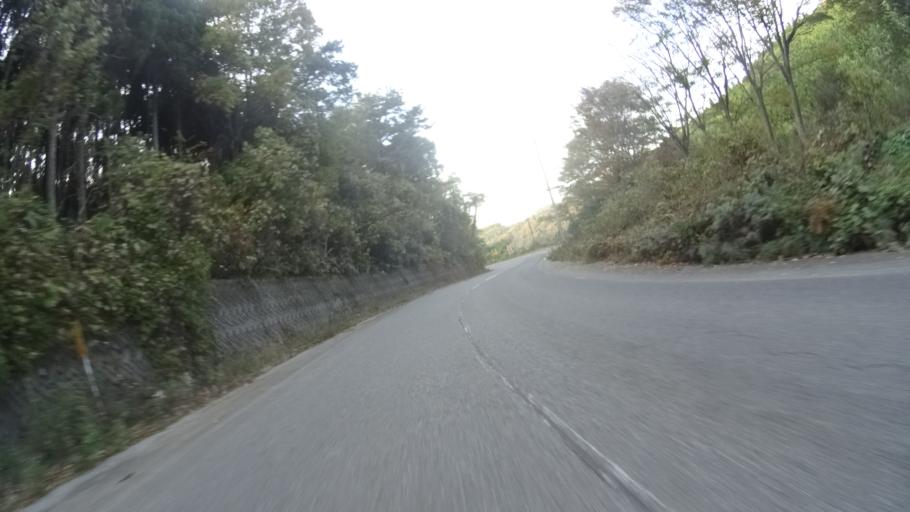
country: JP
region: Ishikawa
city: Nanao
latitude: 37.2092
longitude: 136.7078
